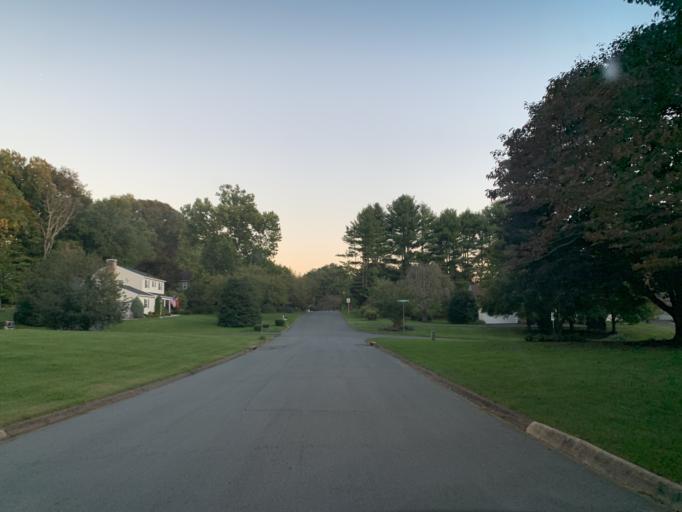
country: US
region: Maryland
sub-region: Harford County
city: South Bel Air
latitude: 39.5302
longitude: -76.3141
